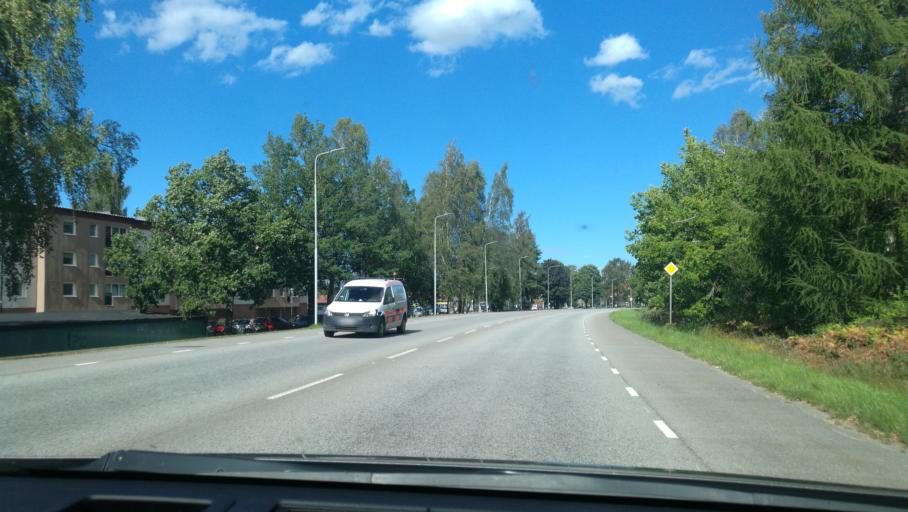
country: SE
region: Vaestra Goetaland
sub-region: Mariestads Kommun
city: Mariestad
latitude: 58.6945
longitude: 13.8158
